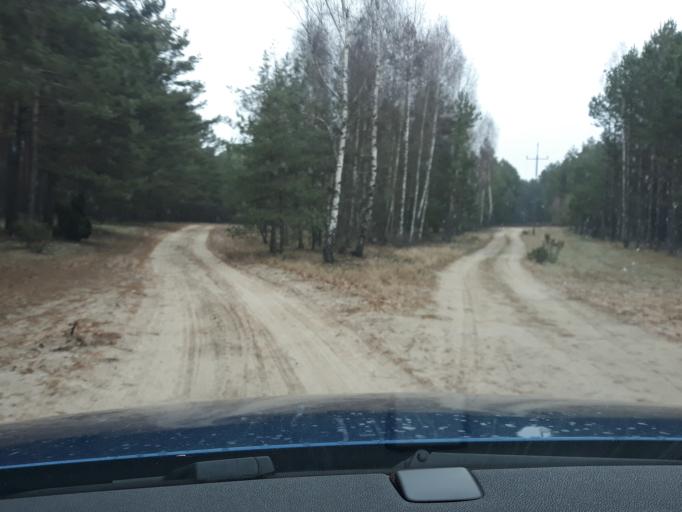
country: PL
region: Pomeranian Voivodeship
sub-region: Powiat chojnicki
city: Chojnice
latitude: 53.8605
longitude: 17.5453
